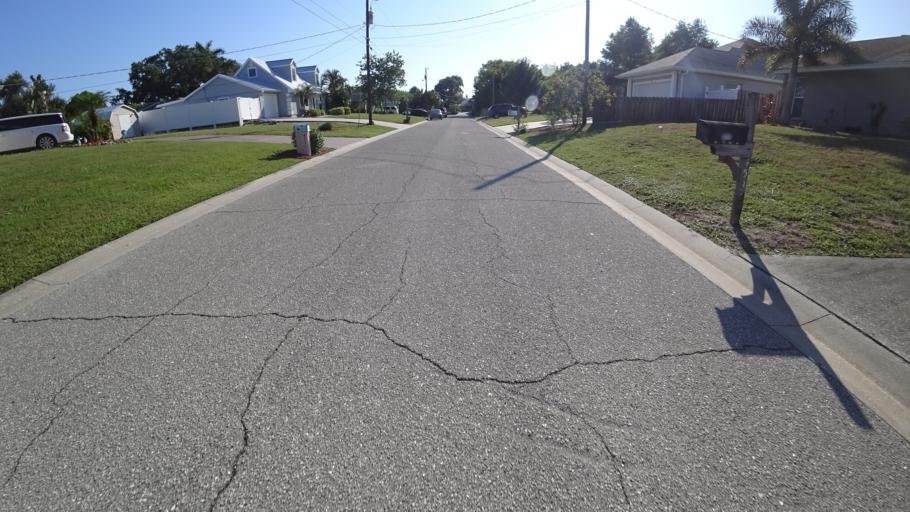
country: US
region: Florida
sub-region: Manatee County
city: Ellenton
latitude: 27.5017
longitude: -82.5060
